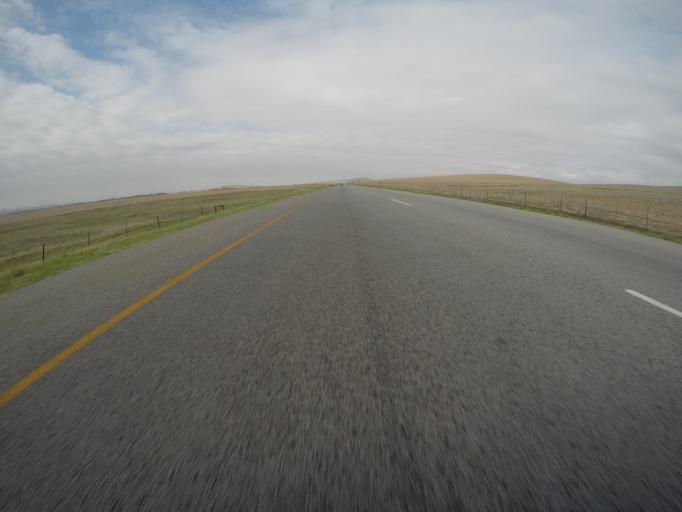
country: ZA
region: Western Cape
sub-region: City of Cape Town
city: Sunset Beach
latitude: -33.7264
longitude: 18.4847
